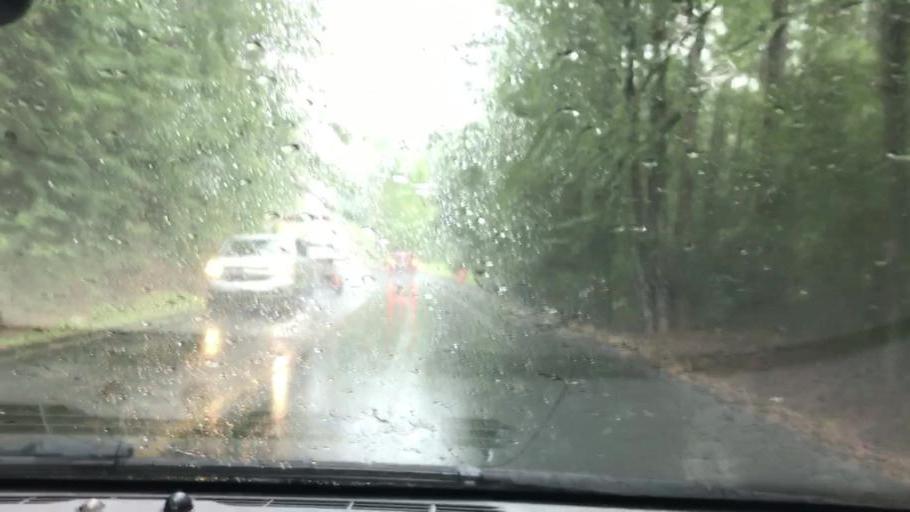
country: US
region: Georgia
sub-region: Clay County
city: Fort Gaines
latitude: 31.5486
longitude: -85.0187
